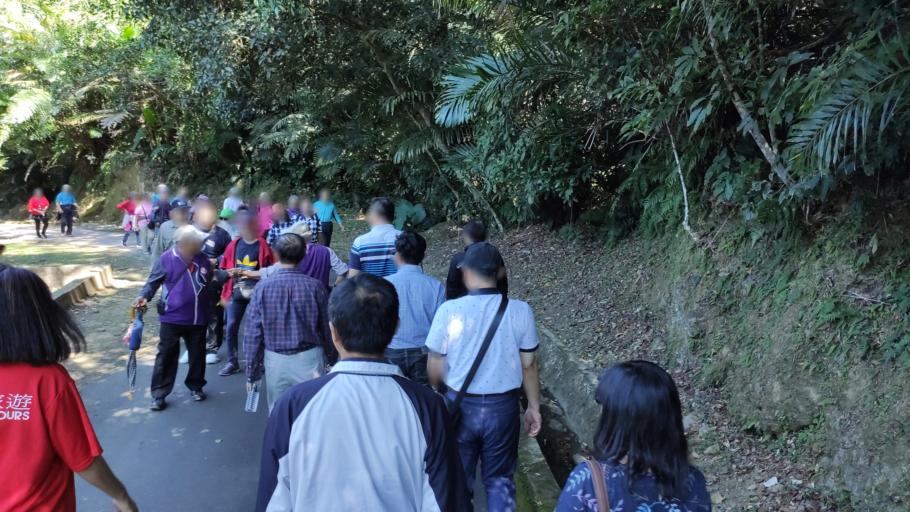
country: TW
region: Taiwan
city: Daxi
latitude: 24.8405
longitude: 121.3071
